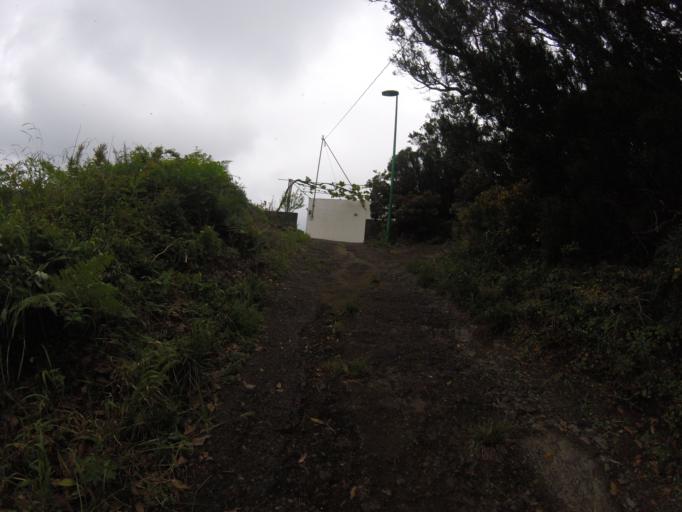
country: ES
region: Canary Islands
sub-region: Provincia de Santa Cruz de Tenerife
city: Tegueste
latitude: 28.5438
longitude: -16.2810
